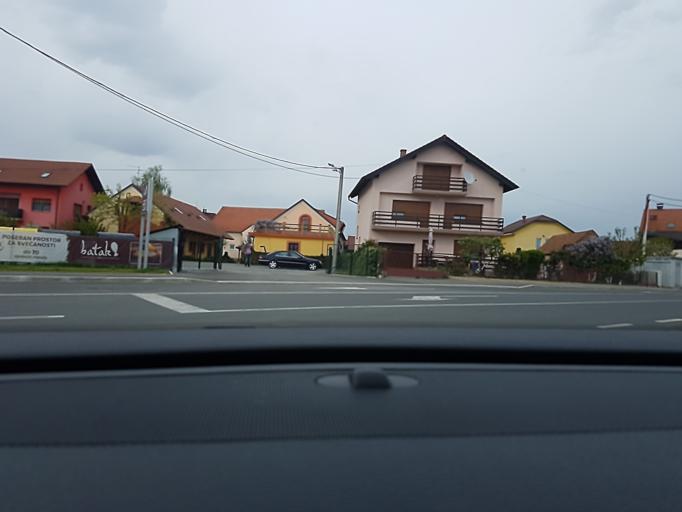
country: HR
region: Zagrebacka
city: Zapresic
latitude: 45.8519
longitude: 15.8077
